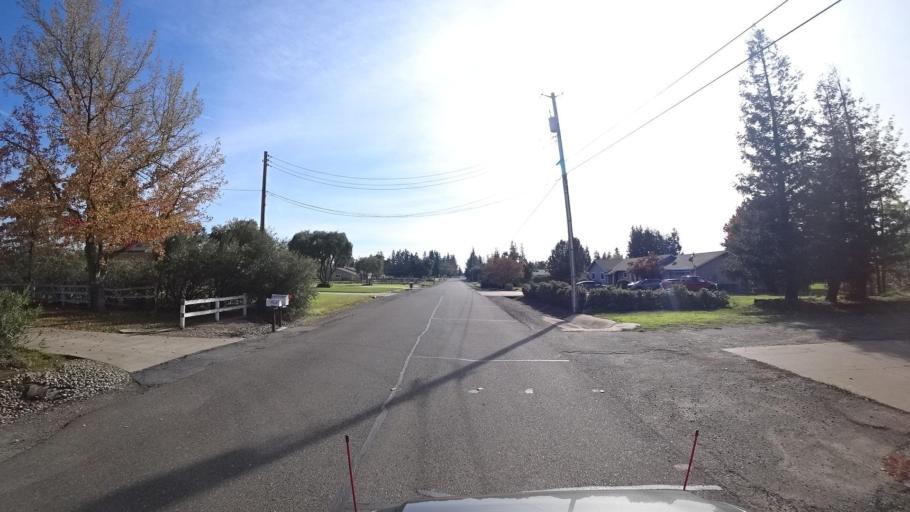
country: US
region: California
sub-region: Sacramento County
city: Vineyard
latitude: 38.4402
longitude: -121.3610
